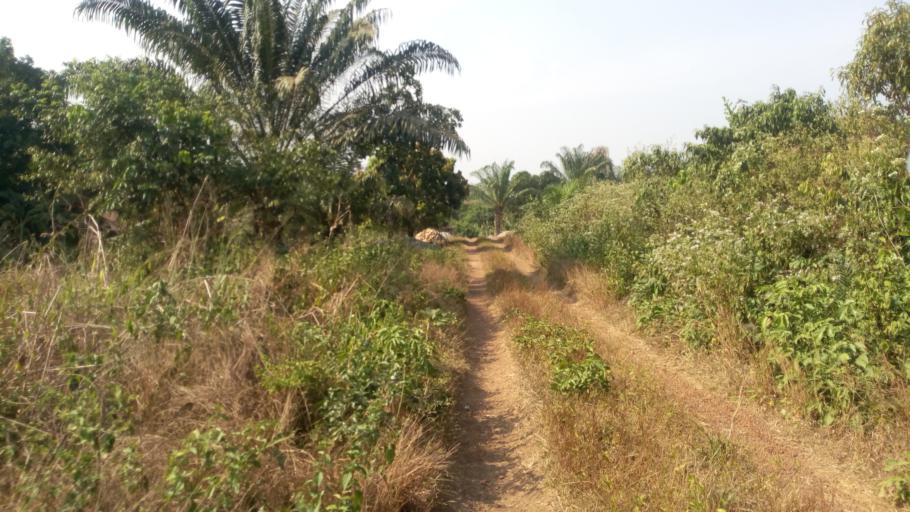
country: SL
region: Southern Province
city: Mogbwemo
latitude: 7.6159
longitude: -12.1824
